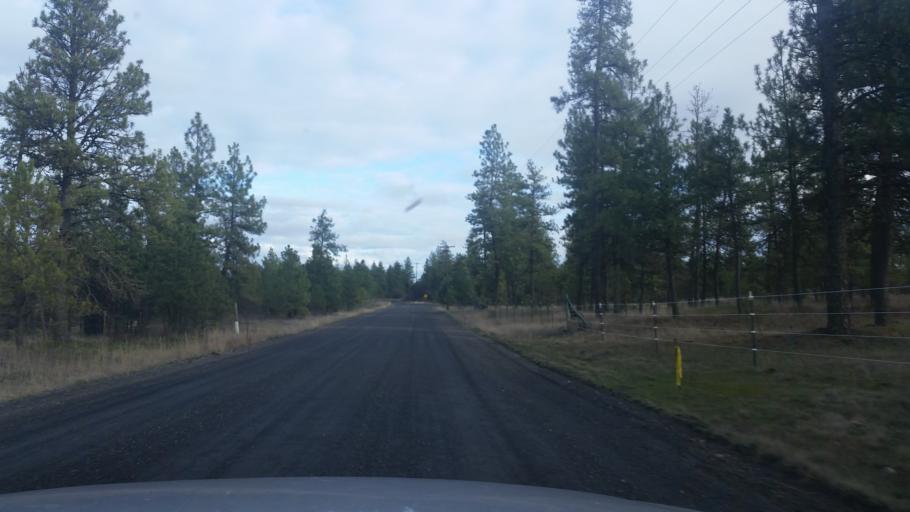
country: US
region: Washington
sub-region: Spokane County
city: Cheney
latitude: 47.4346
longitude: -117.4609
